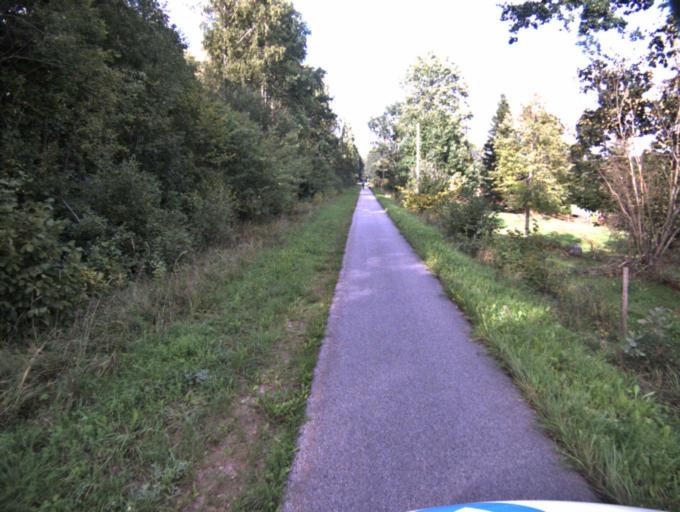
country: SE
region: Vaestra Goetaland
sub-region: Ulricehamns Kommun
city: Ulricehamn
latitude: 57.9068
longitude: 13.4725
